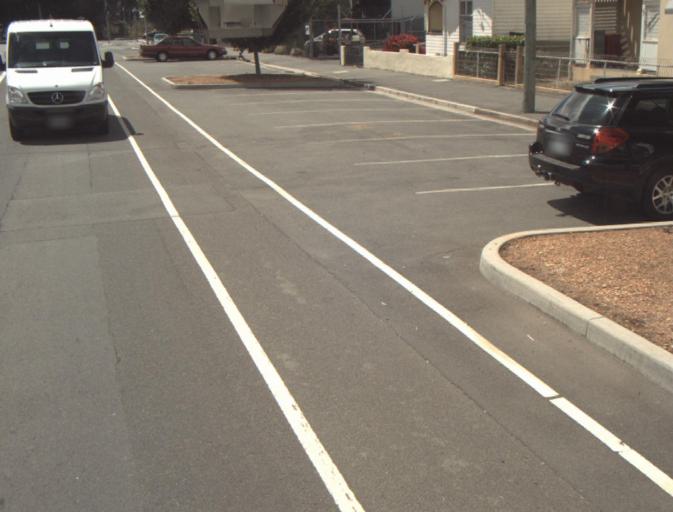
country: AU
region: Tasmania
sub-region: Launceston
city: Launceston
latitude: -41.4246
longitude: 147.1354
